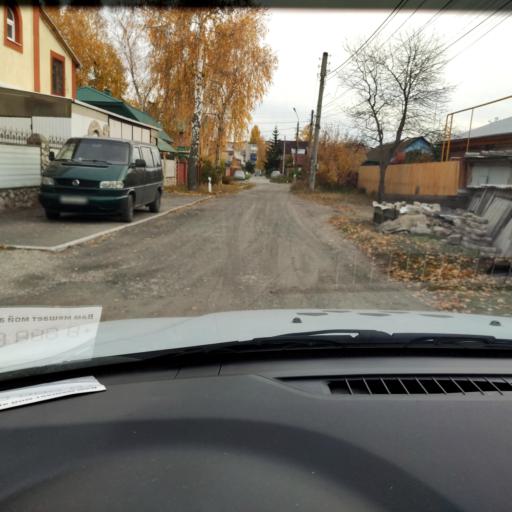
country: RU
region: Samara
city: Tol'yatti
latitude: 53.5324
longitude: 49.3992
